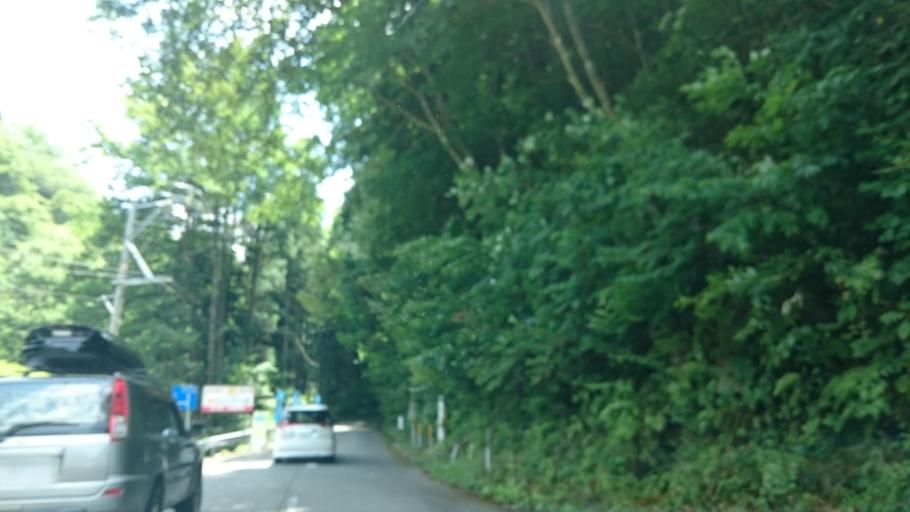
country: JP
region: Gifu
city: Takayama
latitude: 35.9203
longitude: 137.3217
